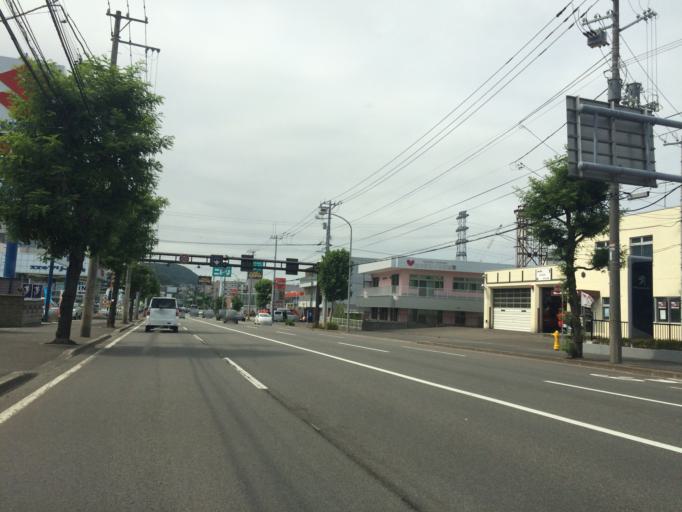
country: JP
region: Hokkaido
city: Sapporo
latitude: 43.0951
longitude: 141.2613
